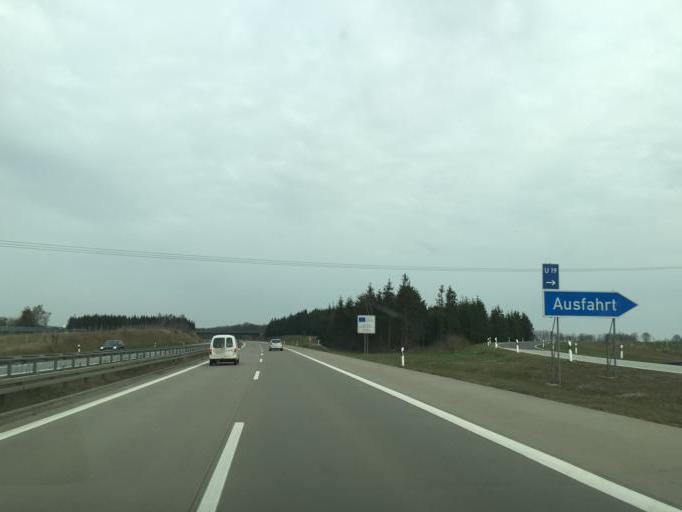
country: DE
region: Mecklenburg-Vorpommern
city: Laage
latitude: 53.8843
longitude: 12.2589
